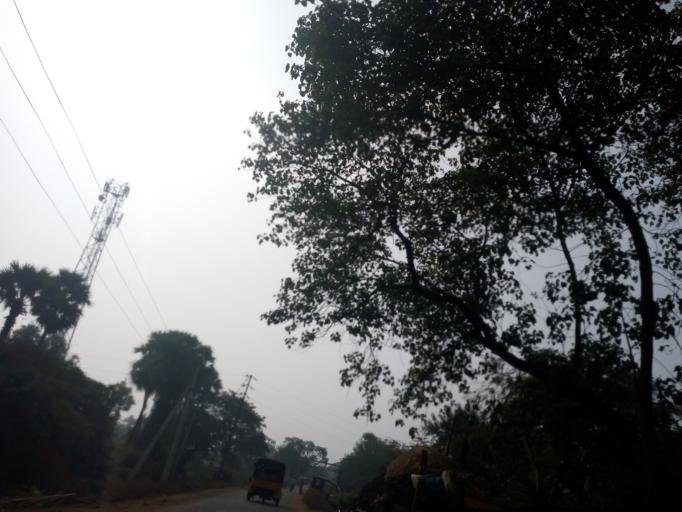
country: IN
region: Andhra Pradesh
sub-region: West Godavari
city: Tadepallegudem
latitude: 16.8164
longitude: 81.3628
